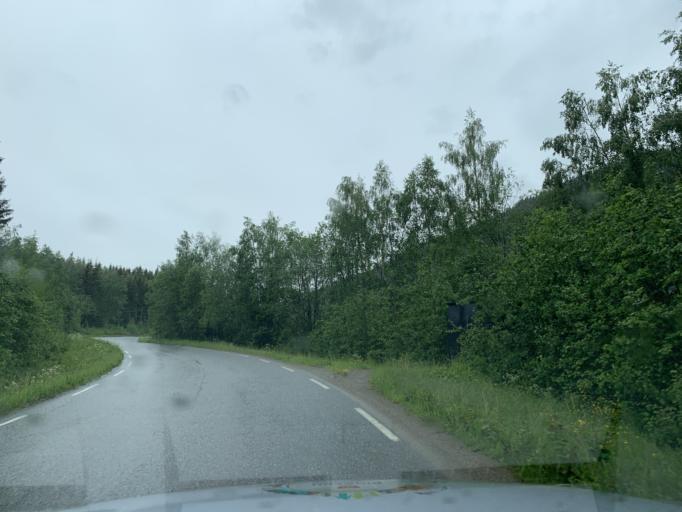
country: NO
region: Oppland
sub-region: Ringebu
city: Ringebu
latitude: 61.4459
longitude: 10.1702
